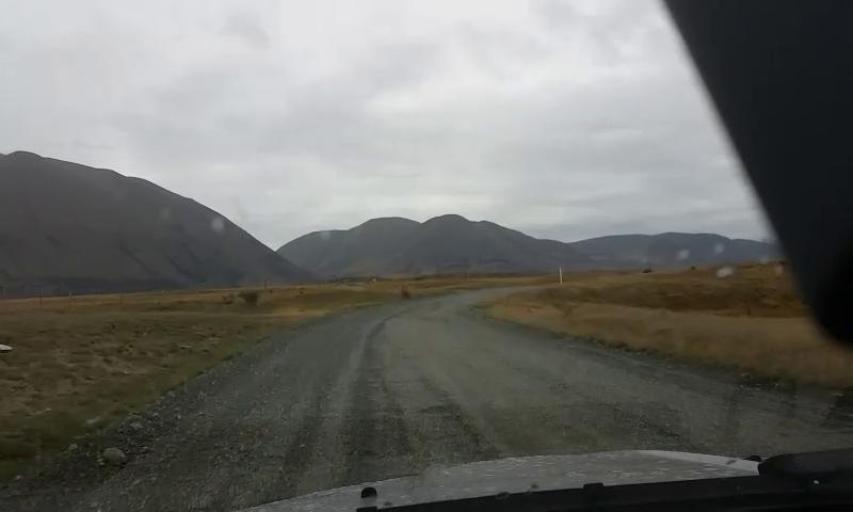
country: NZ
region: Canterbury
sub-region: Ashburton District
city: Methven
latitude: -43.6151
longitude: 171.1072
